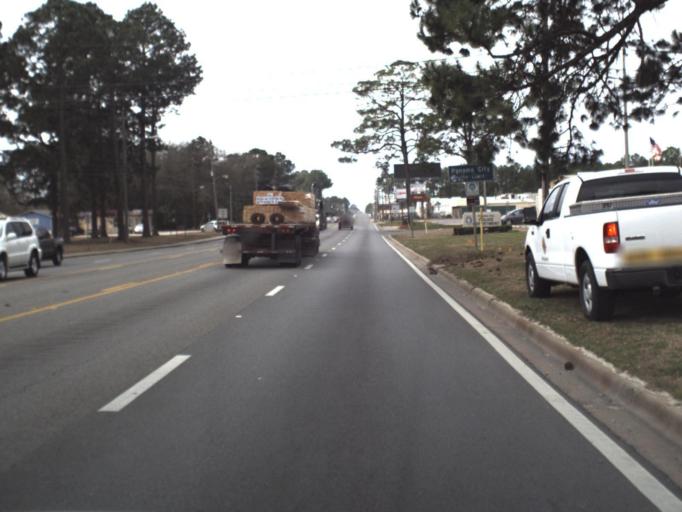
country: US
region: Florida
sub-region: Bay County
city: Cedar Grove
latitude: 30.1751
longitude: -85.6405
